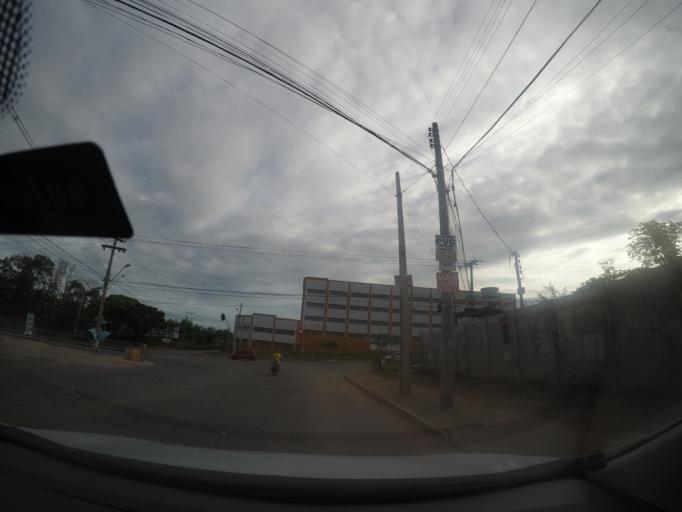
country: BR
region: Goias
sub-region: Goiania
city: Goiania
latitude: -16.6644
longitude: -49.3185
